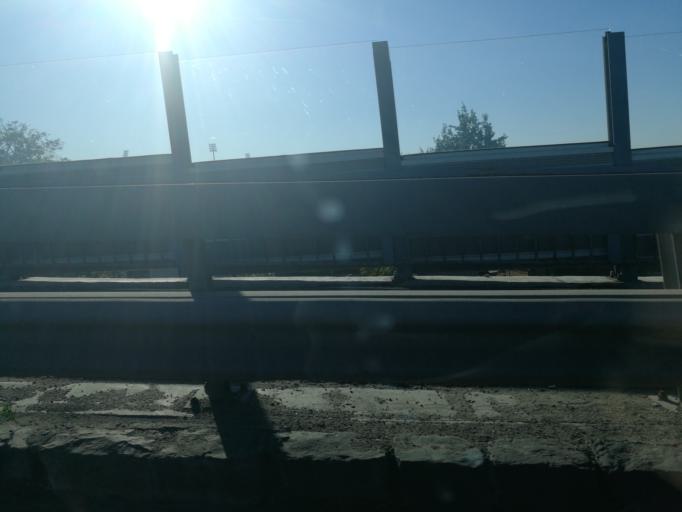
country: RO
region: Brasov
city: Brasov
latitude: 45.6676
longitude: 25.5915
